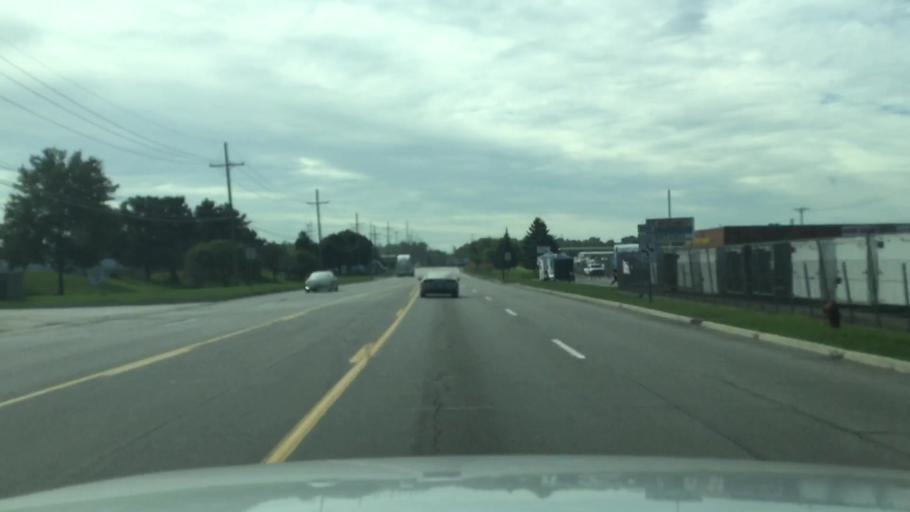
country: US
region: Michigan
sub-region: Wayne County
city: Canton
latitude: 42.2677
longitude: -83.4872
